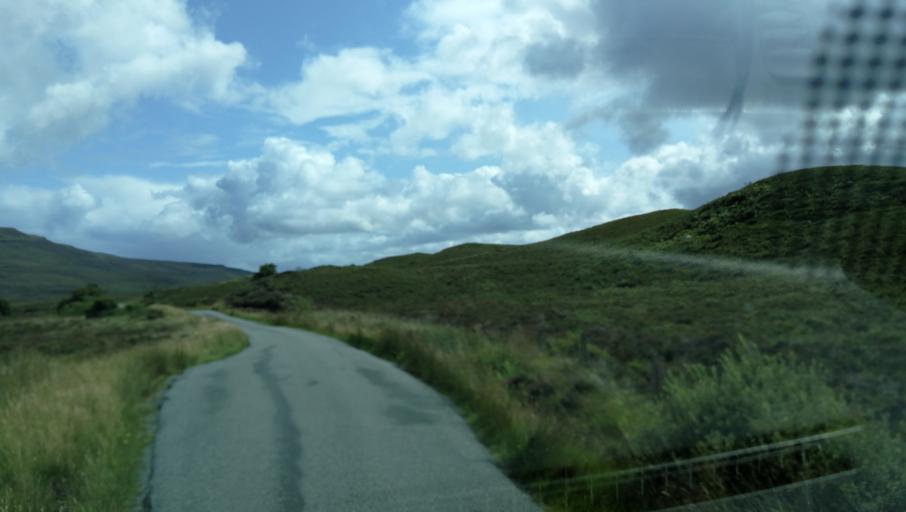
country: GB
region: Scotland
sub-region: Highland
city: Portree
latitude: 57.3849
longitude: -6.1911
